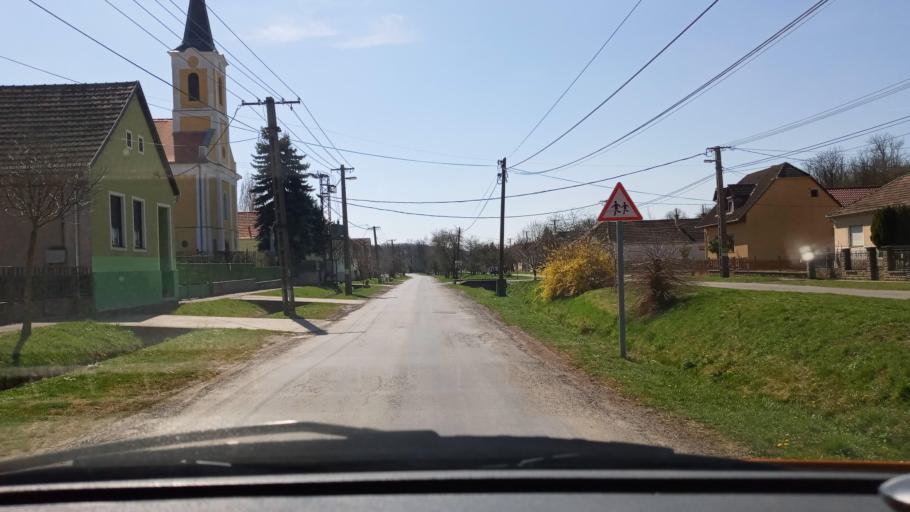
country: HU
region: Baranya
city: Pecsvarad
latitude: 46.0617
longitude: 18.4506
